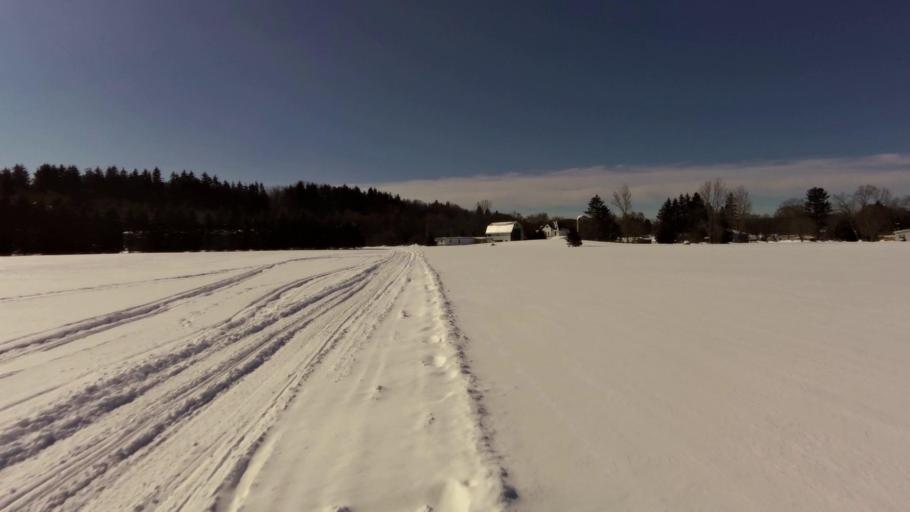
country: US
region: New York
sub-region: Cattaraugus County
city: Franklinville
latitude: 42.3450
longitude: -78.4481
